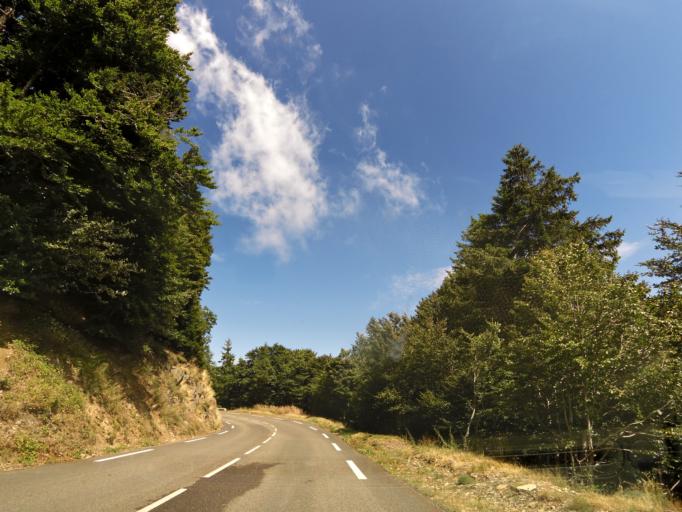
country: FR
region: Languedoc-Roussillon
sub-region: Departement du Gard
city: Valleraugue
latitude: 44.1040
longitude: 3.5440
